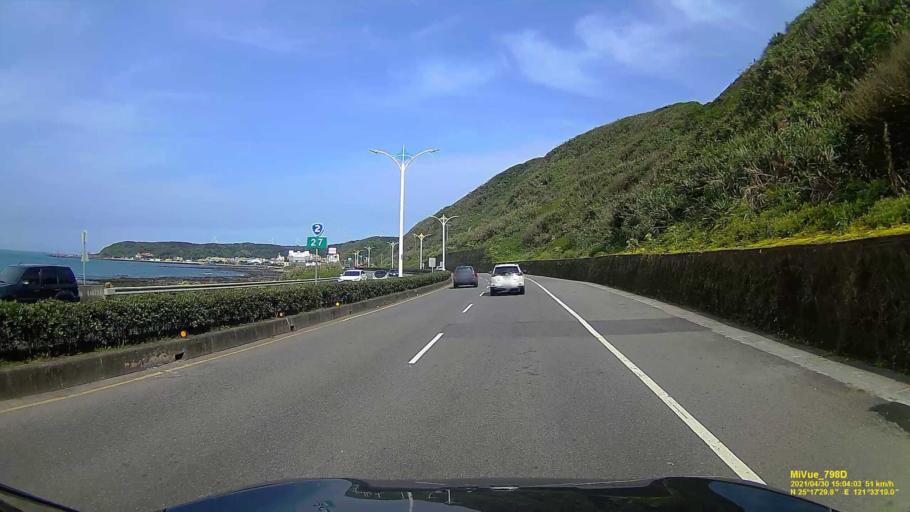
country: TW
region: Taipei
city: Taipei
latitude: 25.2915
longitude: 121.5555
